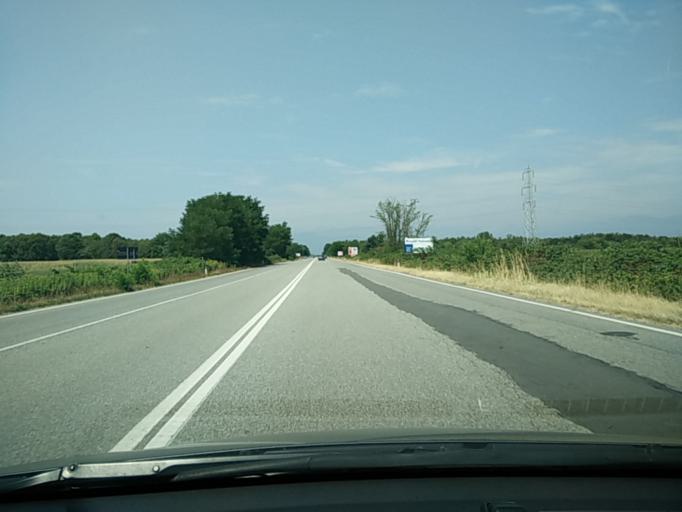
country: IT
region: Piedmont
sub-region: Provincia di Torino
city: Volpiano
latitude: 45.1882
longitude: 7.7654
